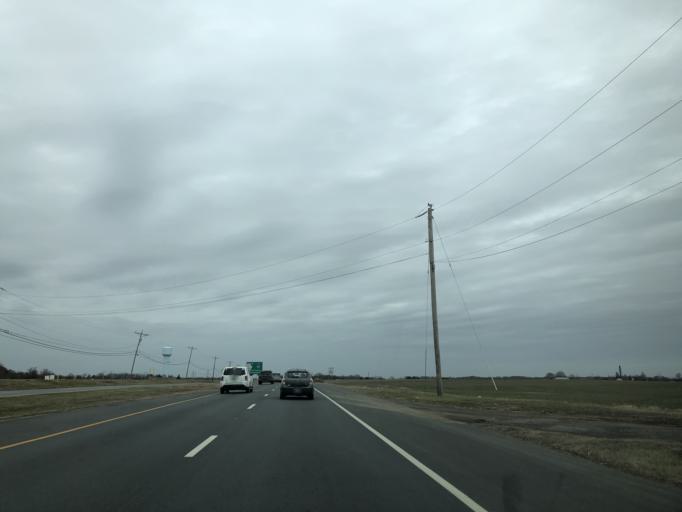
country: US
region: Delaware
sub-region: New Castle County
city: Delaware City
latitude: 39.5119
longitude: -75.6490
